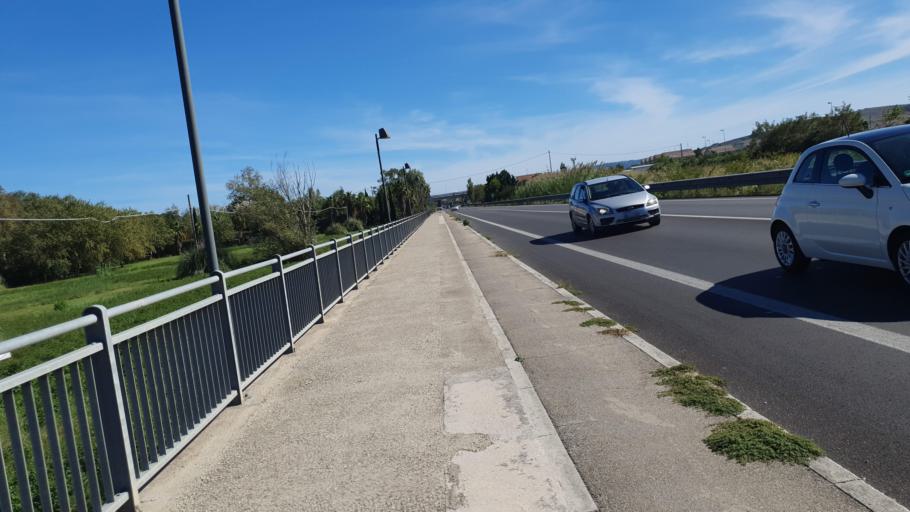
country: IT
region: Abruzzo
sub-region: Provincia di Chieti
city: Salvo Marina
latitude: 42.0657
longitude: 14.7779
